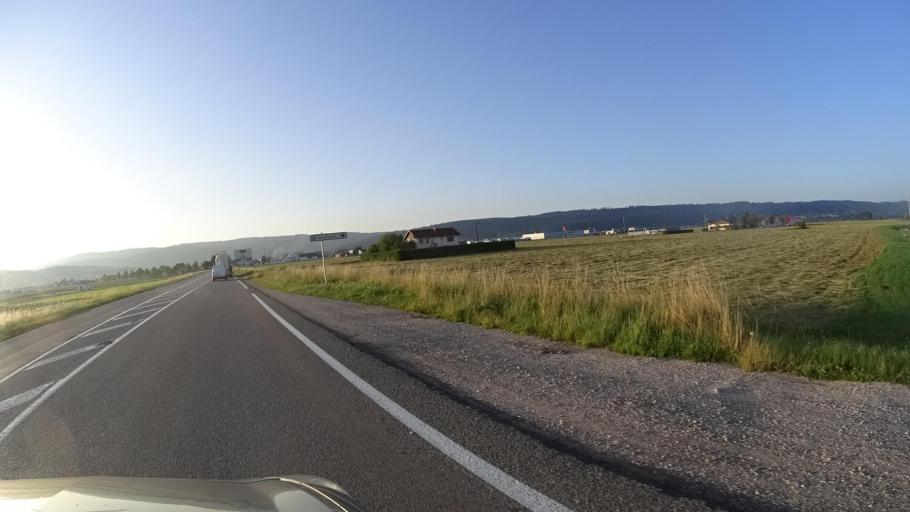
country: FR
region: Franche-Comte
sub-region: Departement du Doubs
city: Doubs
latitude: 46.9118
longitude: 6.3267
